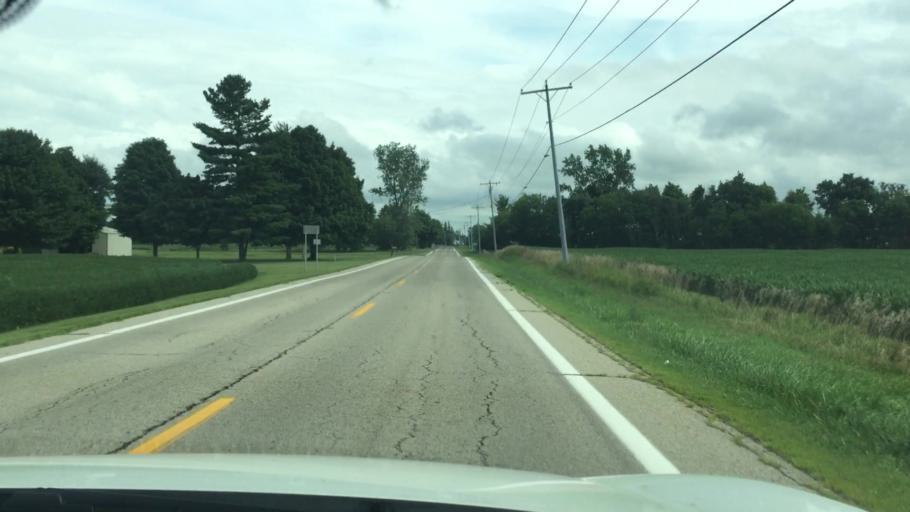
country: US
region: Ohio
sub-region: Champaign County
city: North Lewisburg
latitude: 40.2191
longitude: -83.5497
